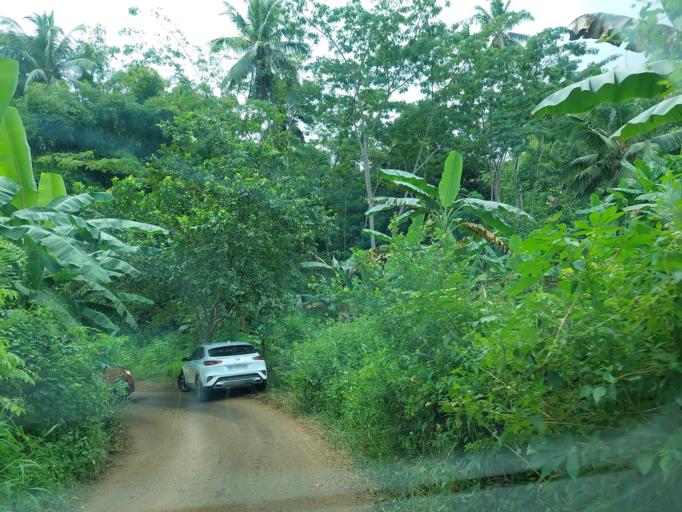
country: YT
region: Tsingoni
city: Tsingoni
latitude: -12.7717
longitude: 45.1119
